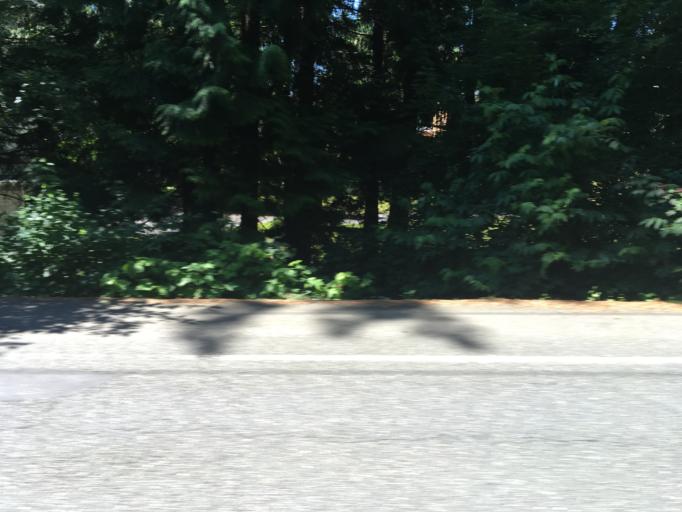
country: US
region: Washington
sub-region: King County
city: Redmond
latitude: 47.6460
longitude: -122.1527
